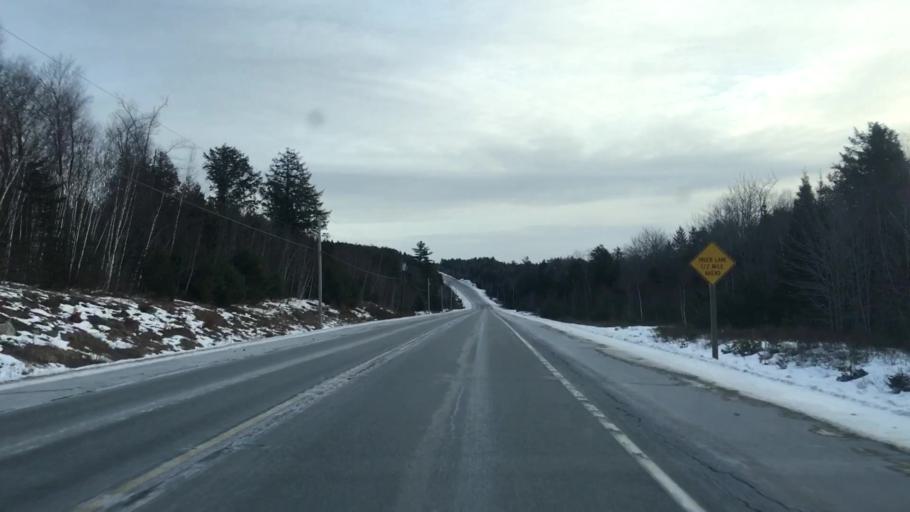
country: US
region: Maine
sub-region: Washington County
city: Cherryfield
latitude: 44.8570
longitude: -68.0456
